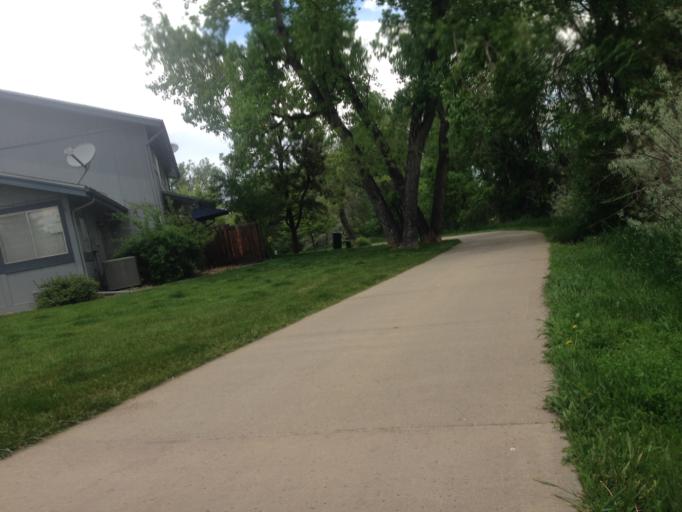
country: US
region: Colorado
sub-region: Boulder County
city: Boulder
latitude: 40.0051
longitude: -105.2397
